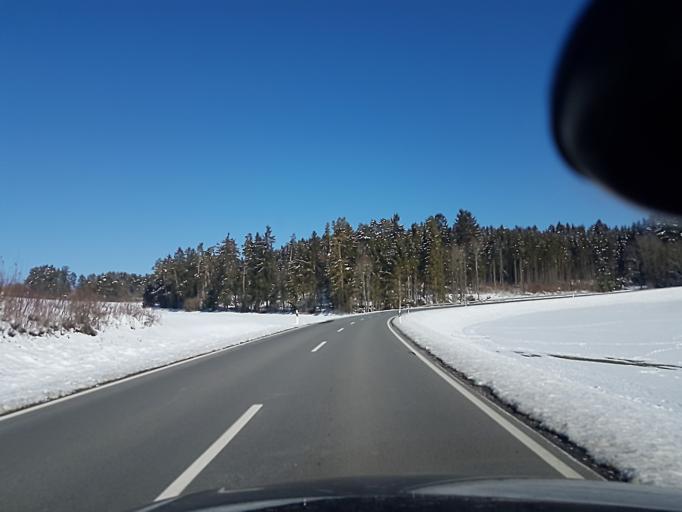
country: DE
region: Baden-Wuerttemberg
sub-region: Freiburg Region
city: Niedereschach
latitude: 48.1689
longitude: 8.5435
